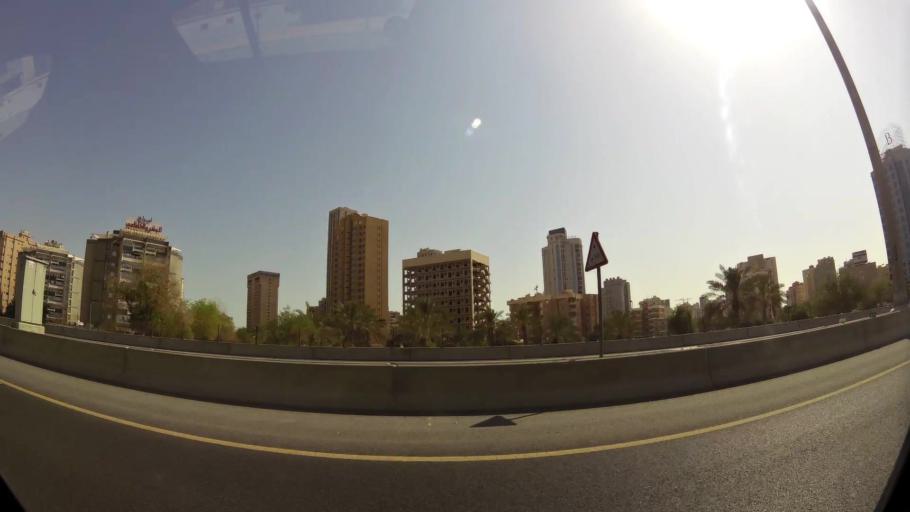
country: KW
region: Al Asimah
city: Ad Dasmah
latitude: 29.3768
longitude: 47.9968
